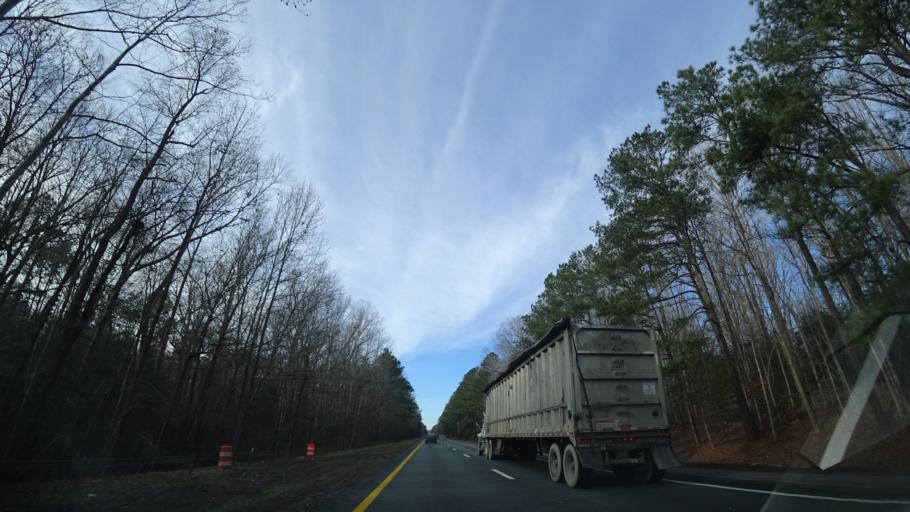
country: US
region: Virginia
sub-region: New Kent County
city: New Kent
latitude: 37.4814
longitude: -76.9374
